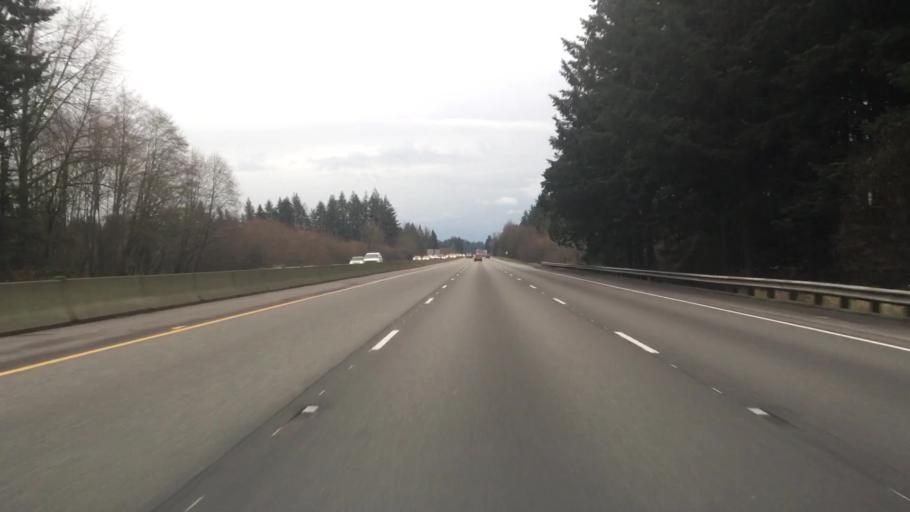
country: US
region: Washington
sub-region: Thurston County
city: Tumwater
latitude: 46.9406
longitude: -122.9412
